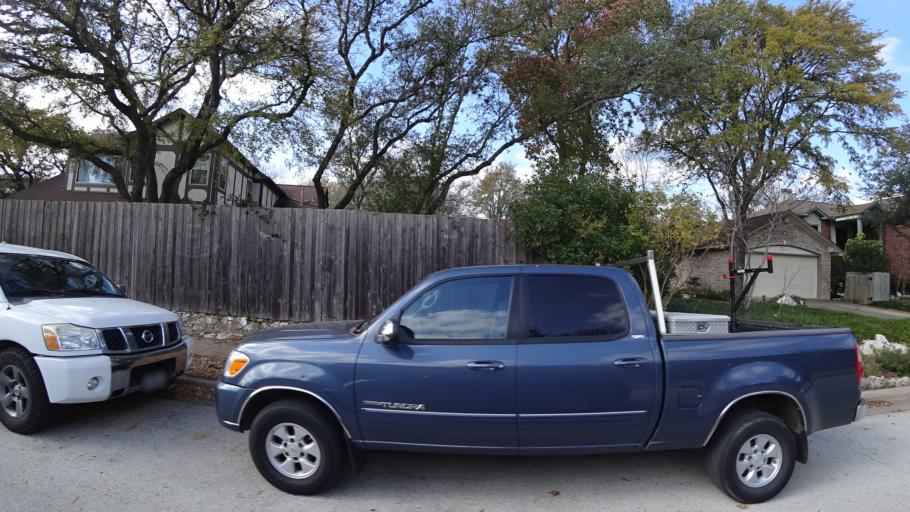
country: US
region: Texas
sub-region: Travis County
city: Shady Hollow
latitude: 30.1654
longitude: -97.8536
